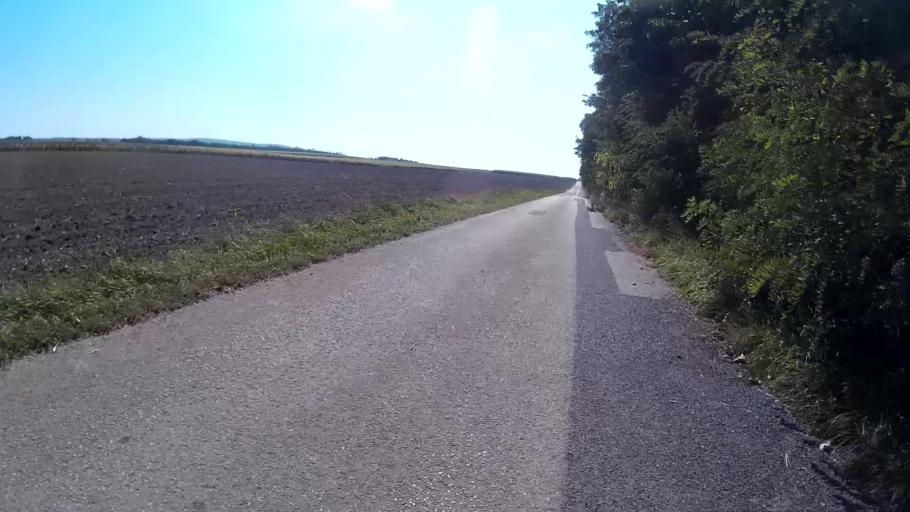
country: AT
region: Lower Austria
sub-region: Politischer Bezirk Mistelbach
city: Neudorf bei Staatz
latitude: 48.7714
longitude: 16.4882
